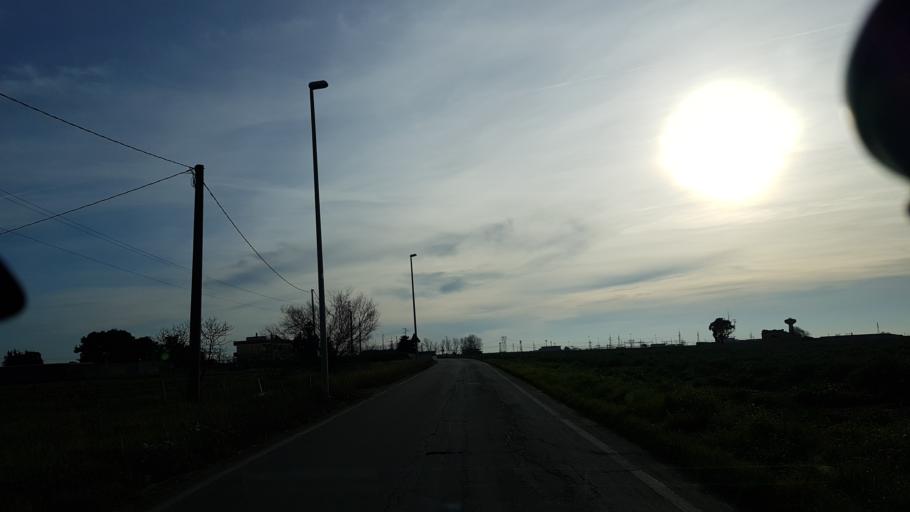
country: IT
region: Apulia
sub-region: Provincia di Brindisi
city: Brindisi
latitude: 40.6124
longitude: 17.9147
